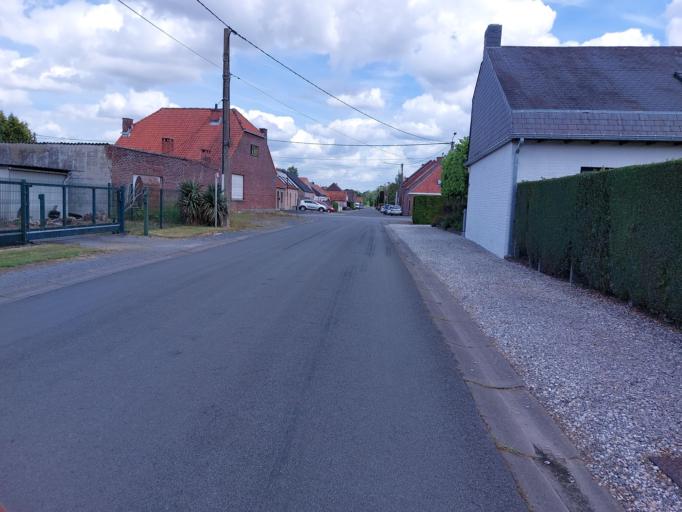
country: BE
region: Wallonia
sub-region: Province du Hainaut
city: Beloeil
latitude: 50.4962
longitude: 3.7582
